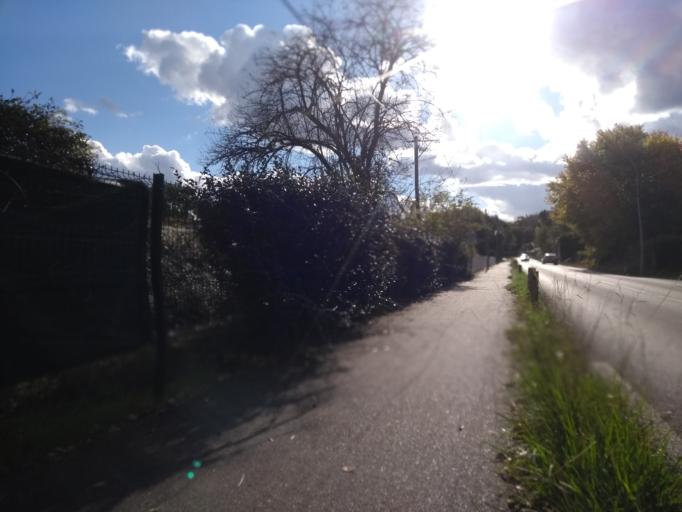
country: FR
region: Aquitaine
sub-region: Departement de la Gironde
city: Cestas
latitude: 44.7471
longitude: -0.6556
